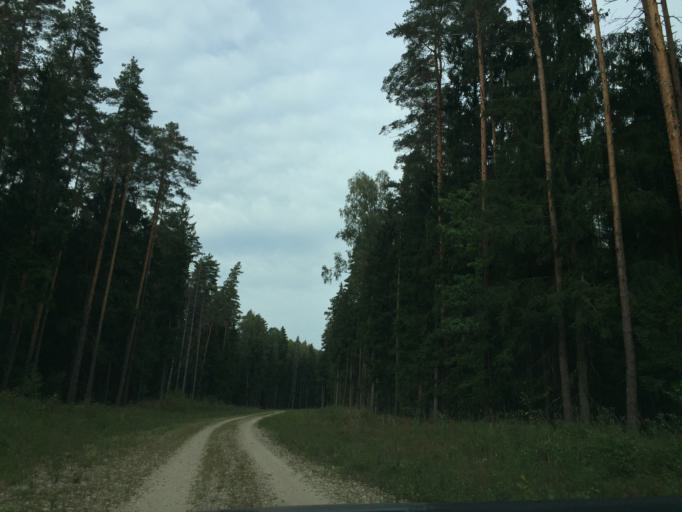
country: LV
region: Baldone
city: Baldone
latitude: 56.7507
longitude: 24.4668
